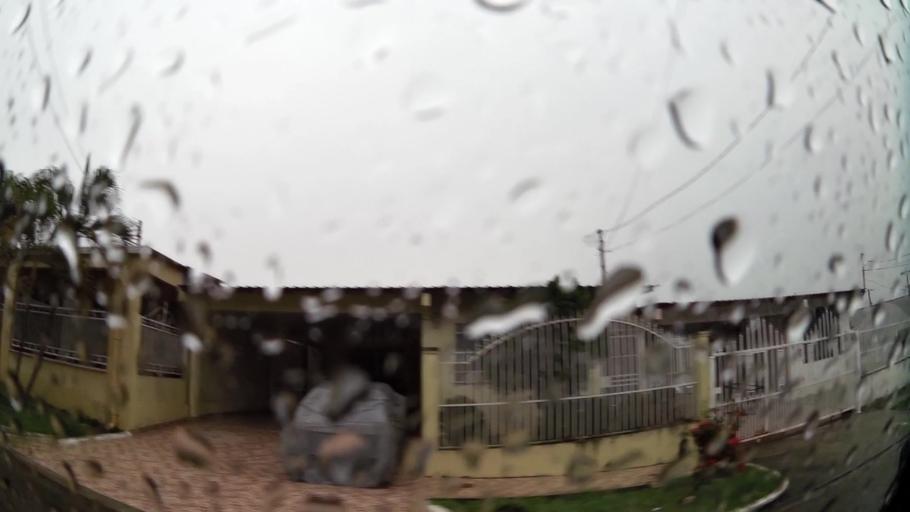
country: PA
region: Panama
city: San Miguelito
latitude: 9.0501
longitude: -79.4678
